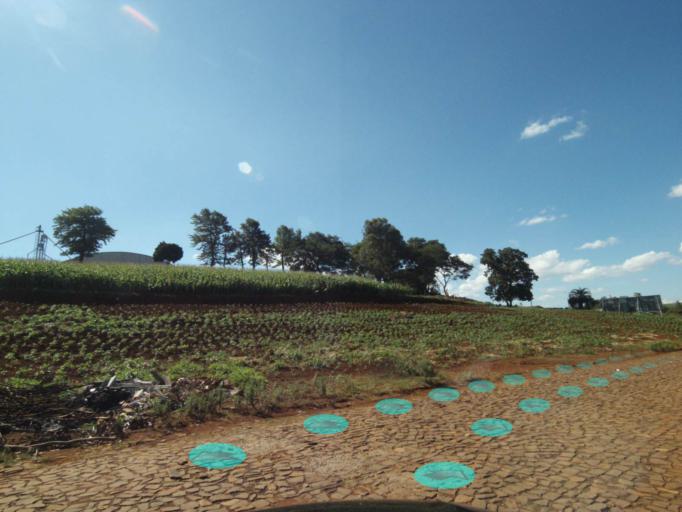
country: BR
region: Parana
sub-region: Coronel Vivida
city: Coronel Vivida
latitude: -26.1419
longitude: -52.3918
